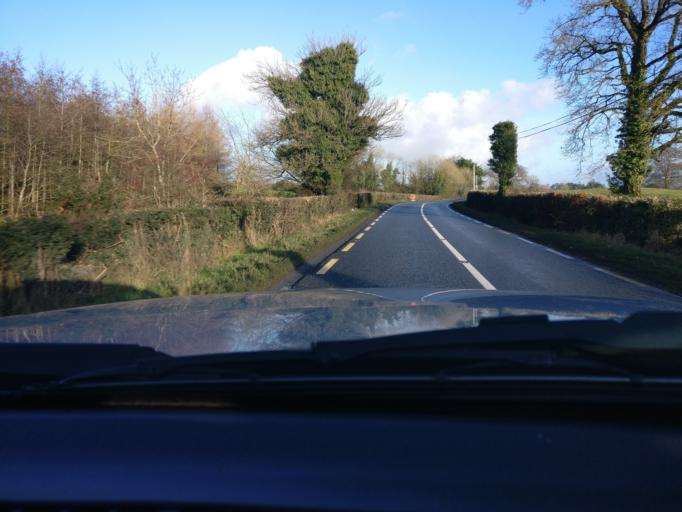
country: IE
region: Leinster
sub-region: An Iarmhi
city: Rathwire
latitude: 53.5740
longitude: -7.1721
